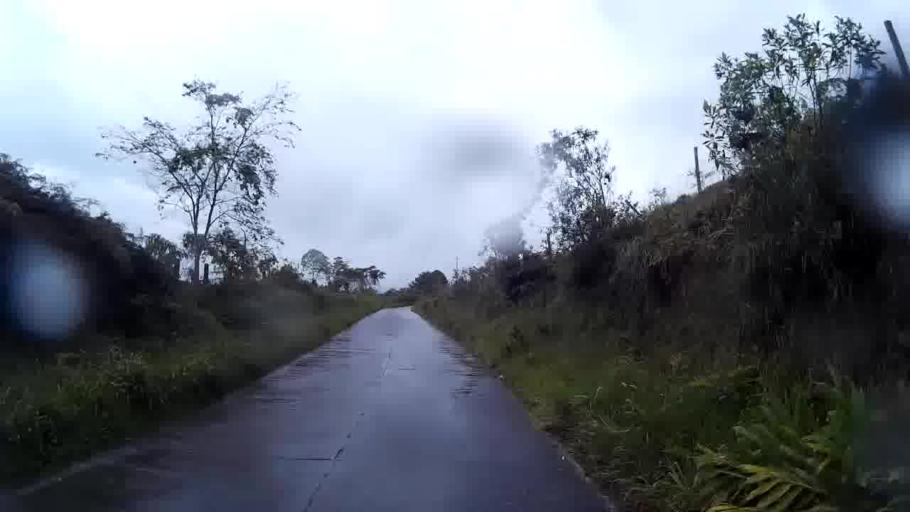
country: CO
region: Quindio
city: Filandia
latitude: 4.6871
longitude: -75.6214
